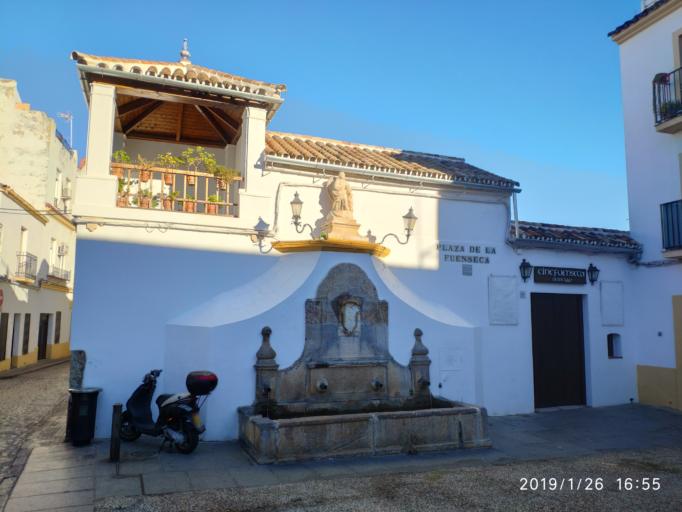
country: ES
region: Andalusia
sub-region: Province of Cordoba
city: Cordoba
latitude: 37.8875
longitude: -4.7754
